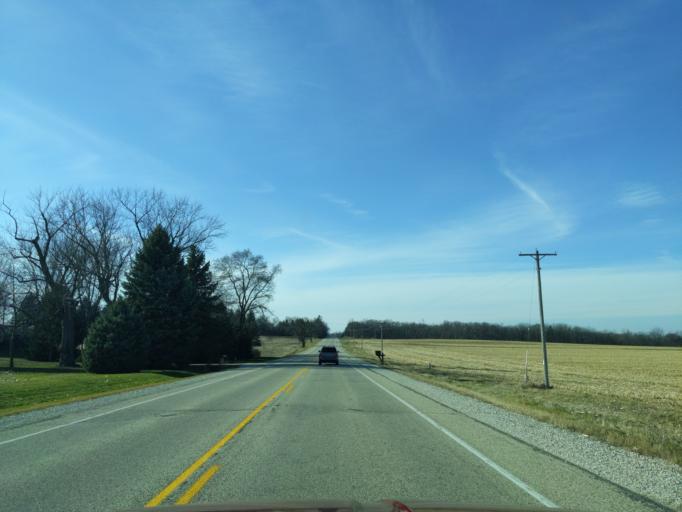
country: US
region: Wisconsin
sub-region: Walworth County
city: Whitewater
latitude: 42.8278
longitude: -88.8052
